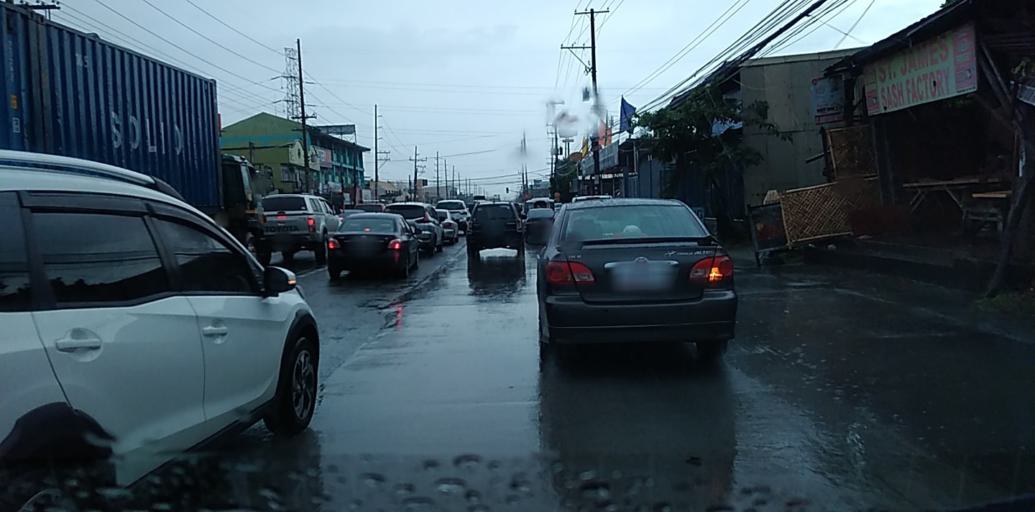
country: PH
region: Central Luzon
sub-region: Province of Pampanga
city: Magliman
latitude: 15.0463
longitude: 120.6703
